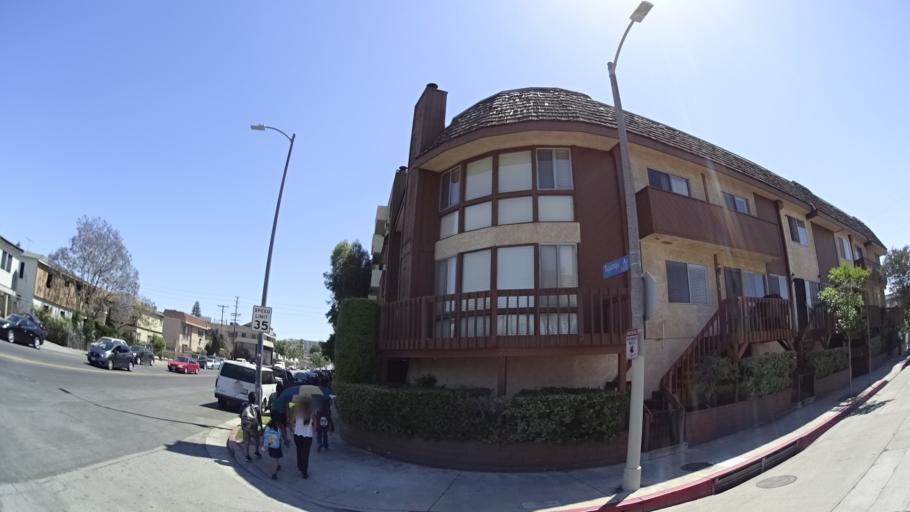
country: US
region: California
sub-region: Los Angeles County
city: North Hollywood
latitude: 34.1766
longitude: -118.3792
